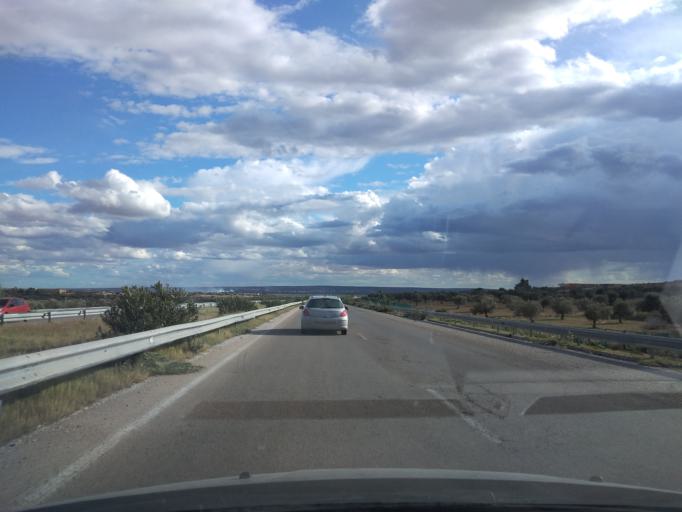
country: TN
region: Al Munastir
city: Manzil Kamil
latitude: 35.5347
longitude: 10.6243
